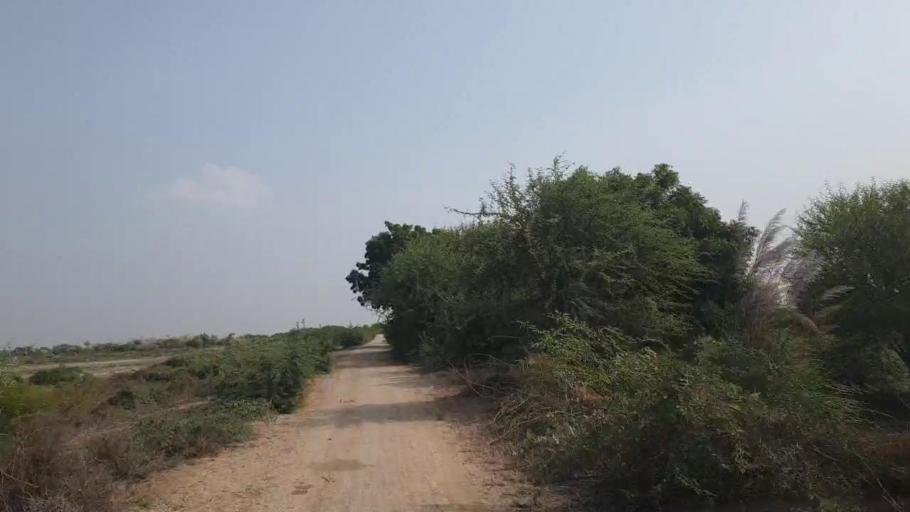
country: PK
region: Sindh
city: Badin
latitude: 24.5475
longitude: 68.6949
